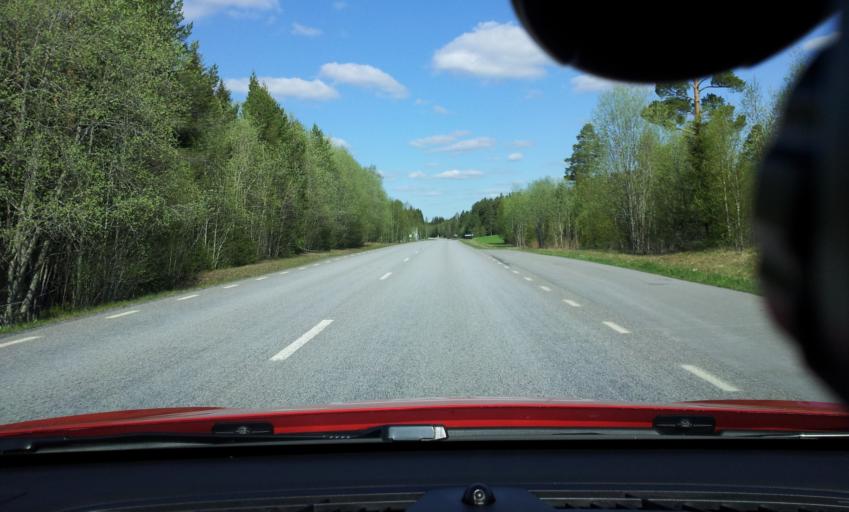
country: SE
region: Jaemtland
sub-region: Krokoms Kommun
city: Valla
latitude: 63.2653
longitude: 13.9660
